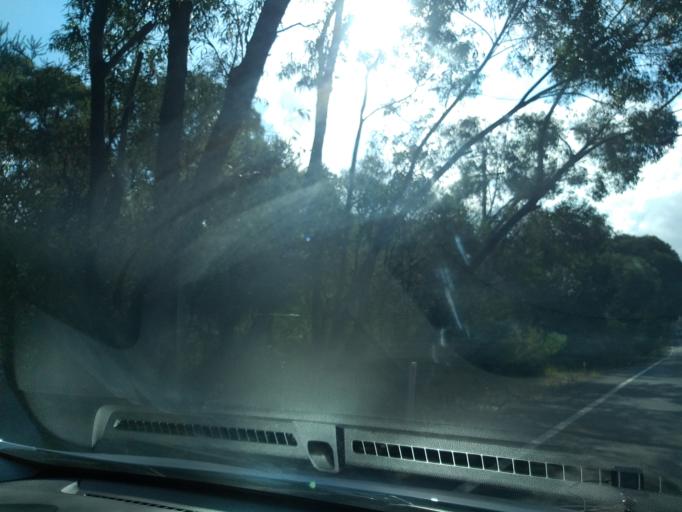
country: AU
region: New South Wales
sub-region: Wollongong
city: Helensburgh
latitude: -34.2152
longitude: 150.9773
